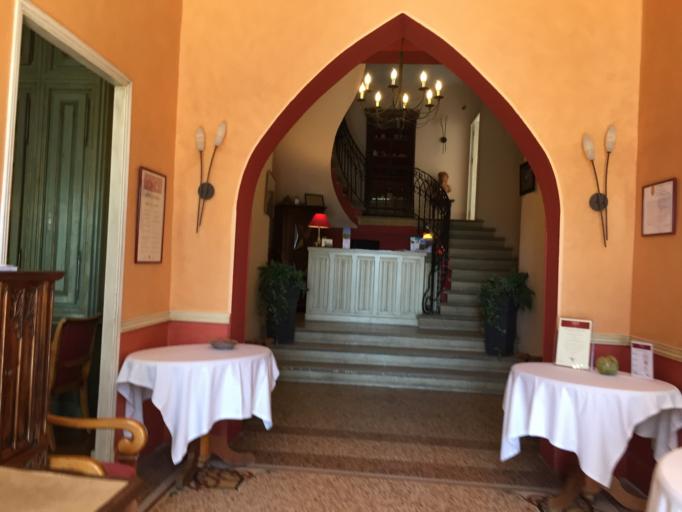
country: FR
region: Provence-Alpes-Cote d'Azur
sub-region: Departement du Vaucluse
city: Chateauneuf-du-Pape
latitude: 44.0500
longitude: 4.8493
